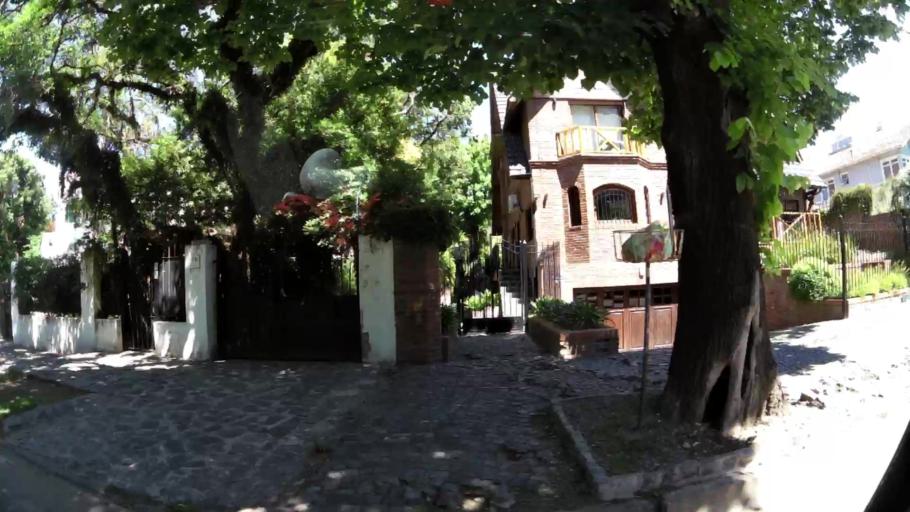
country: AR
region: Buenos Aires
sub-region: Partido de San Isidro
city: San Isidro
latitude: -34.4756
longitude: -58.4941
